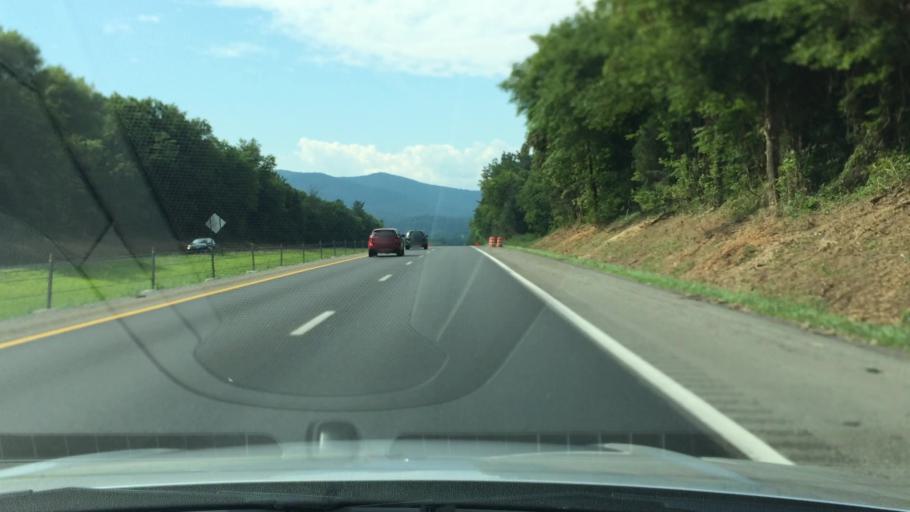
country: US
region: Tennessee
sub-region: Cocke County
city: Newport
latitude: 35.9162
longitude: -83.1875
